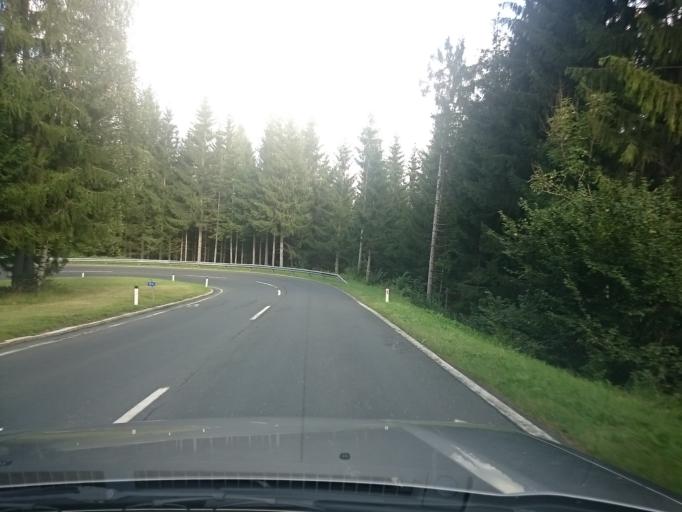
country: AT
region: Carinthia
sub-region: Politischer Bezirk Spittal an der Drau
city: Oberdrauburg
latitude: 46.6598
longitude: 12.9834
